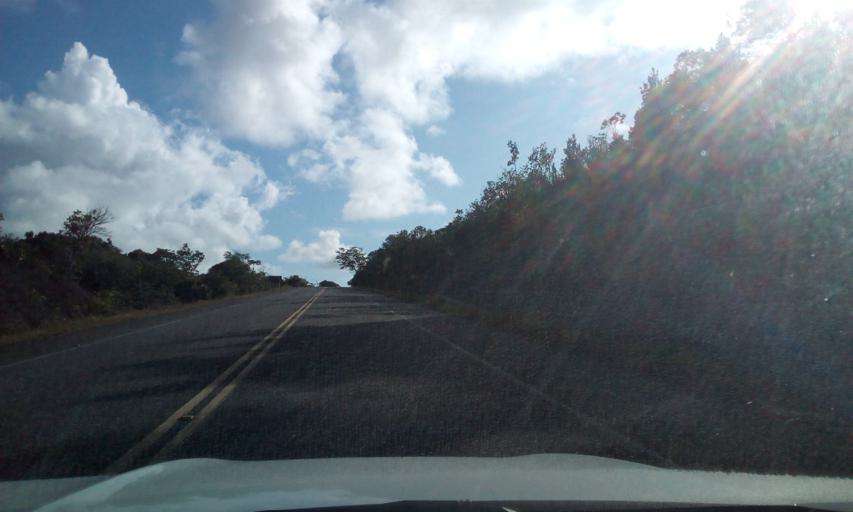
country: BR
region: Bahia
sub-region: Conde
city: Conde
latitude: -12.0843
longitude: -37.7705
